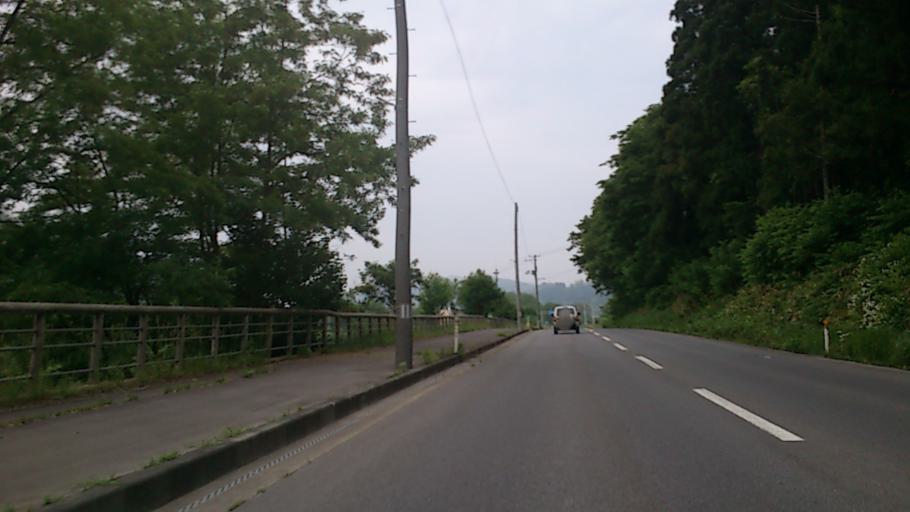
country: JP
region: Aomori
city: Hirosaki
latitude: 40.5950
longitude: 140.3684
